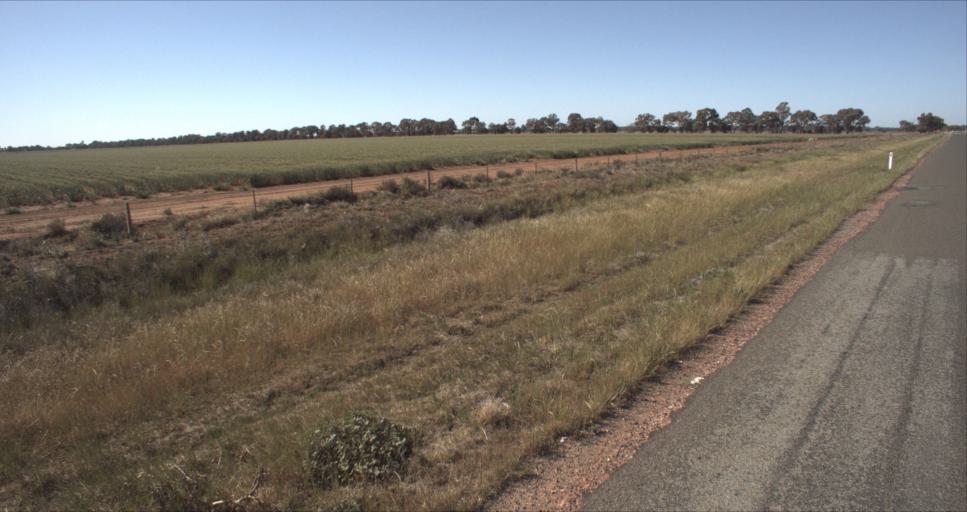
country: AU
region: New South Wales
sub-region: Leeton
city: Leeton
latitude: -34.5742
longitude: 146.2629
